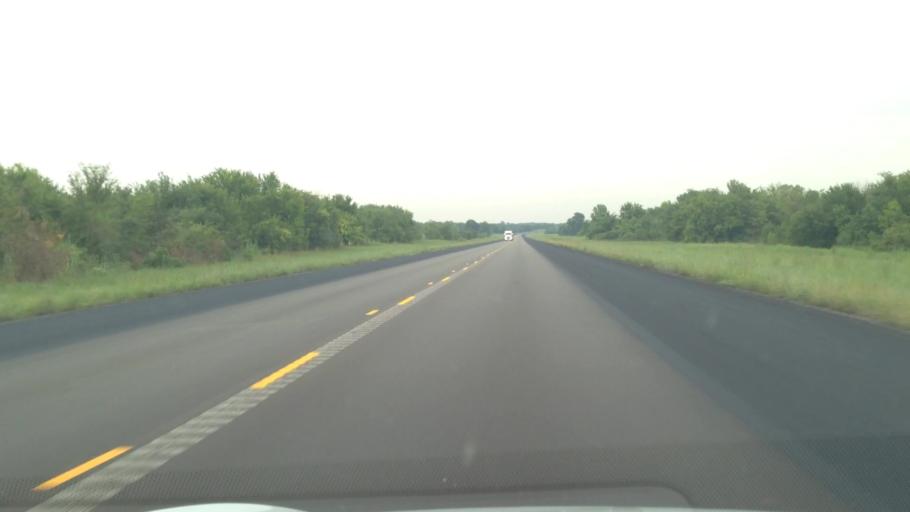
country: US
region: Kansas
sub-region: Cherokee County
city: Baxter Springs
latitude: 37.0383
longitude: -94.7086
